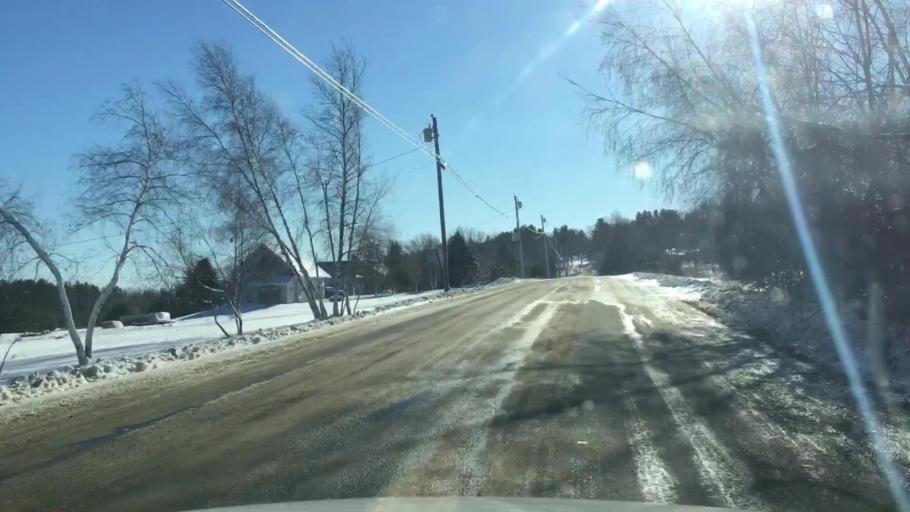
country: US
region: Maine
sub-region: Kennebec County
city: Winthrop
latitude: 44.3435
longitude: -69.9896
